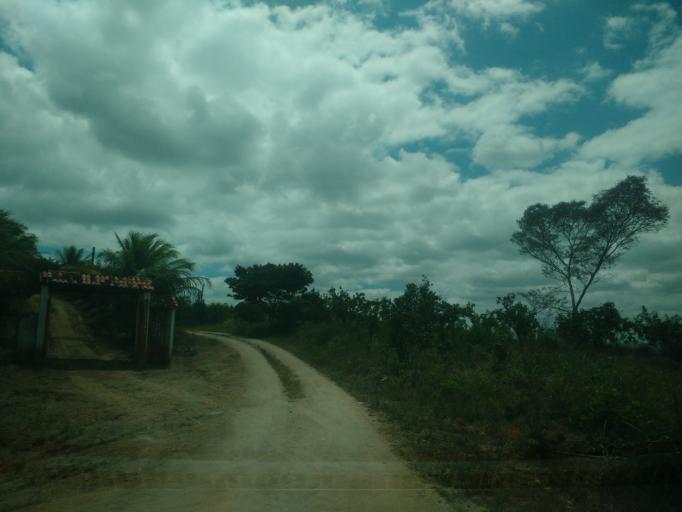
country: BR
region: Alagoas
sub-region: Santana Do Mundau
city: Santana do Mundau
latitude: -9.1580
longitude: -36.1601
